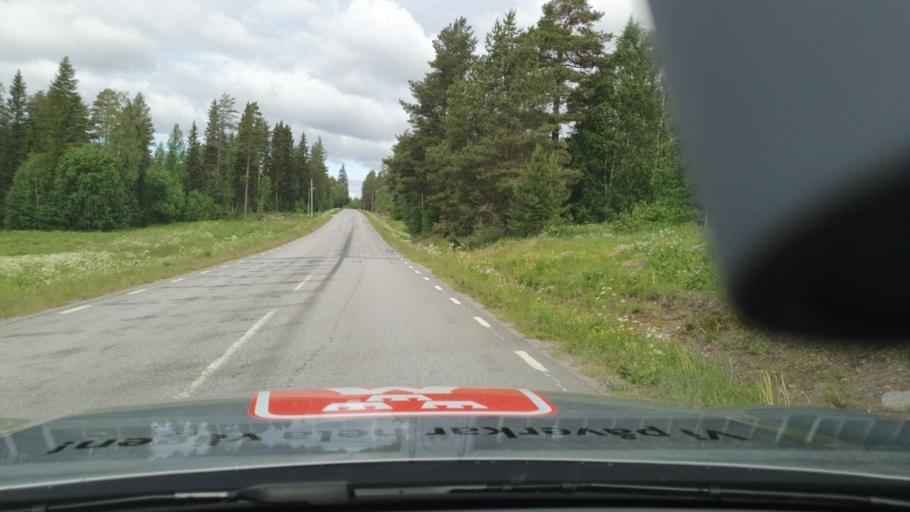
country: SE
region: Norrbotten
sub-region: Lulea Kommun
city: Ranea
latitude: 66.0077
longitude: 22.0126
